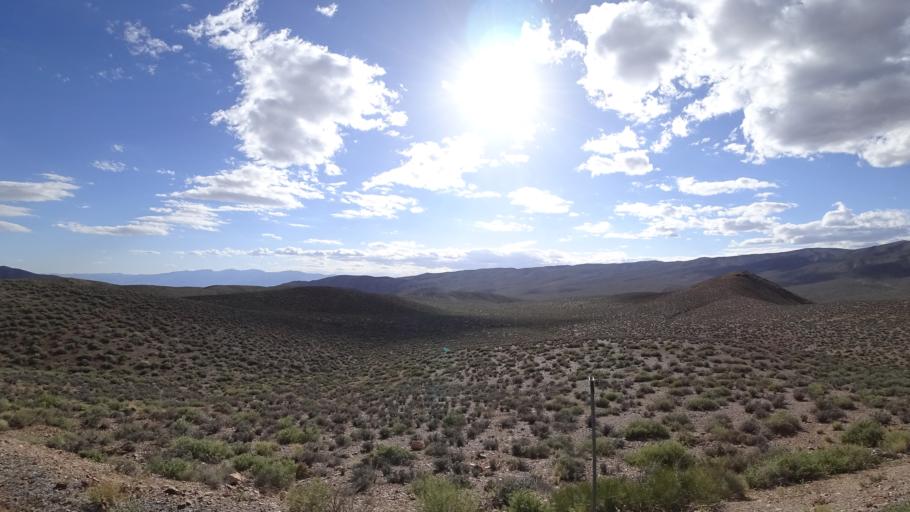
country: US
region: California
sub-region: San Bernardino County
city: Searles Valley
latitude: 36.3189
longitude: -117.1537
